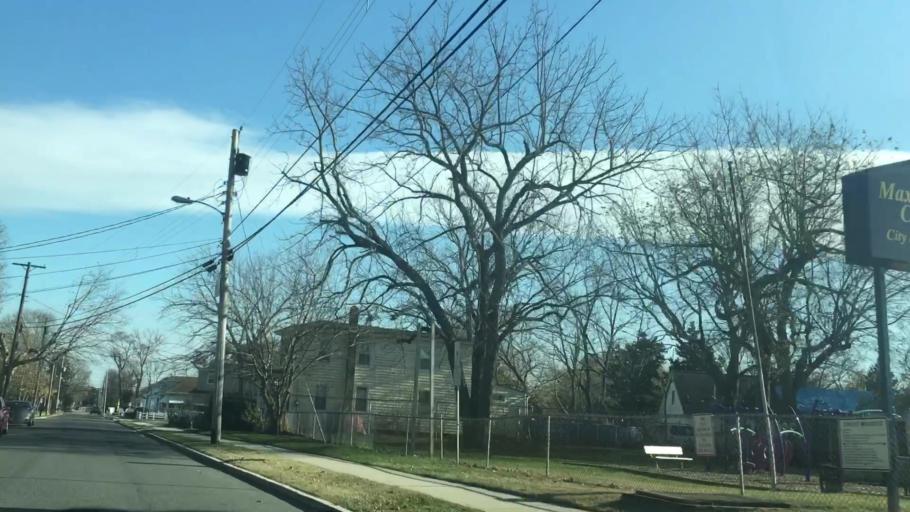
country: US
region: New Jersey
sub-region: Atlantic County
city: Pleasantville
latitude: 39.3879
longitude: -74.5398
